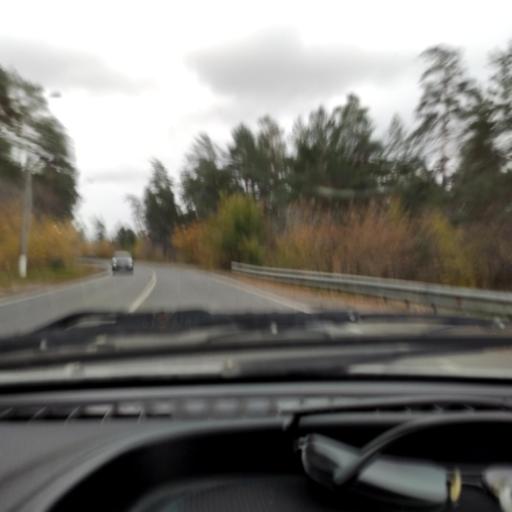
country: RU
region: Samara
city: Tol'yatti
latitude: 53.4737
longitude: 49.3799
